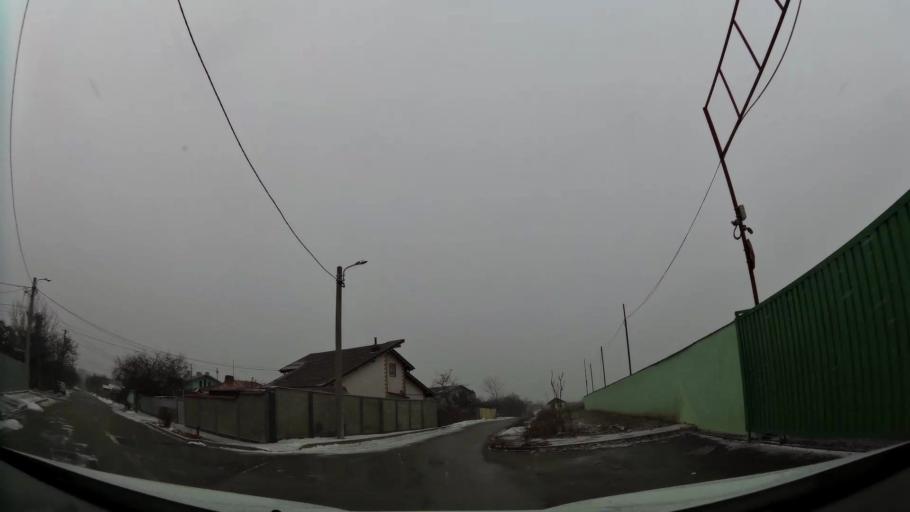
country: RO
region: Prahova
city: Ploiesti
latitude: 44.9558
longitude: 26.0369
